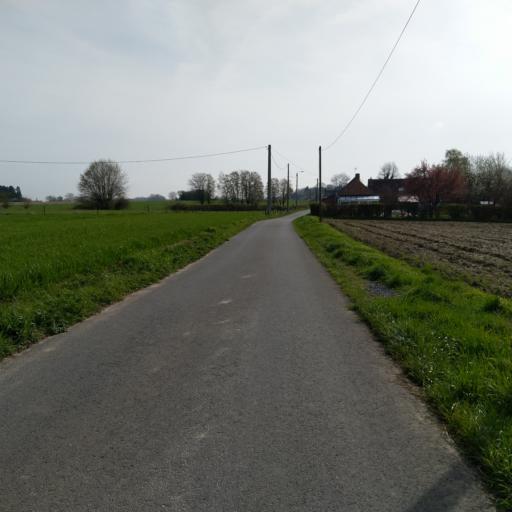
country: FR
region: Nord-Pas-de-Calais
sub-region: Departement du Nord
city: Feignies
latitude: 50.3287
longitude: 3.8825
